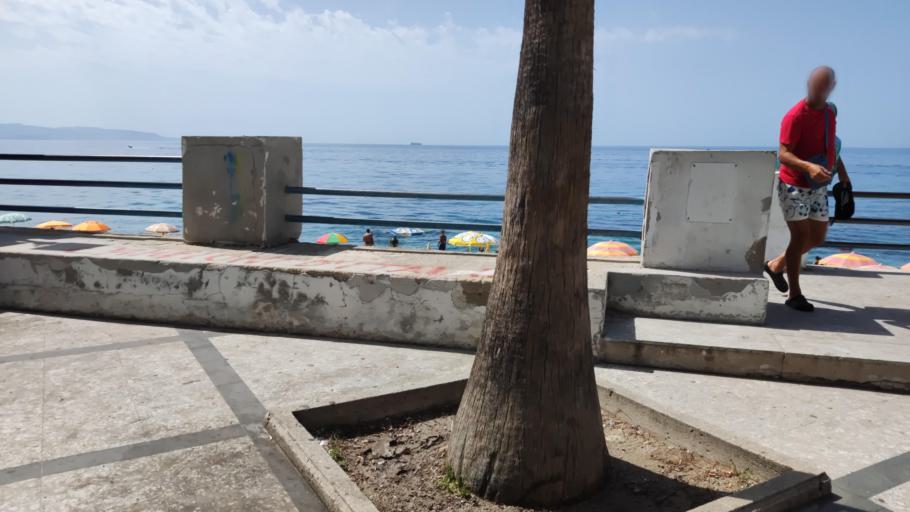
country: IT
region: Calabria
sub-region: Provincia di Reggio Calabria
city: Bagnara Calabra
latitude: 38.2868
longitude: 15.8019
